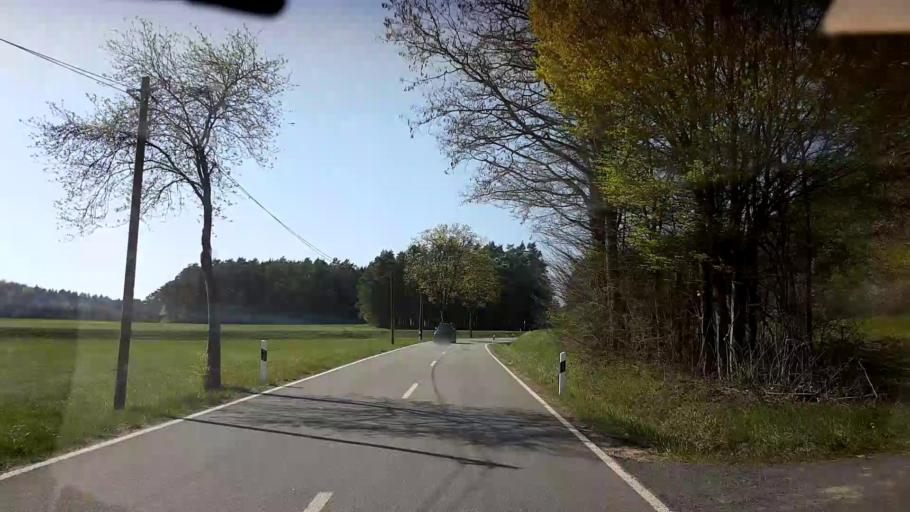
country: DE
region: Bavaria
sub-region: Upper Franconia
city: Pottenstein
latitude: 49.7917
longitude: 11.4139
